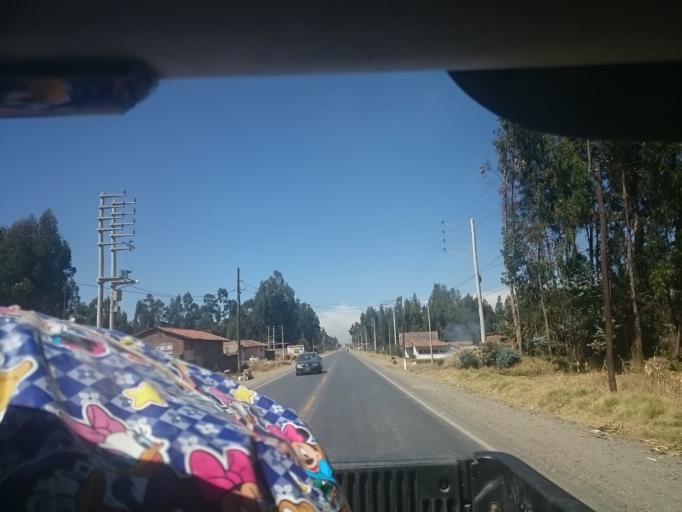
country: PE
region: Junin
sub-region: Provincia de Concepcion
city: Matahuasi
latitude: -11.9049
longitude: -75.3328
